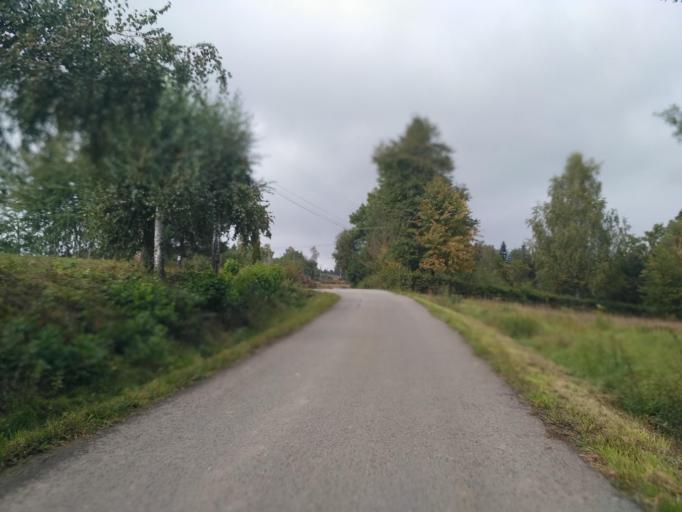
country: PL
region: Subcarpathian Voivodeship
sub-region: Powiat debicki
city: Brzostek
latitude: 49.9444
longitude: 21.4493
